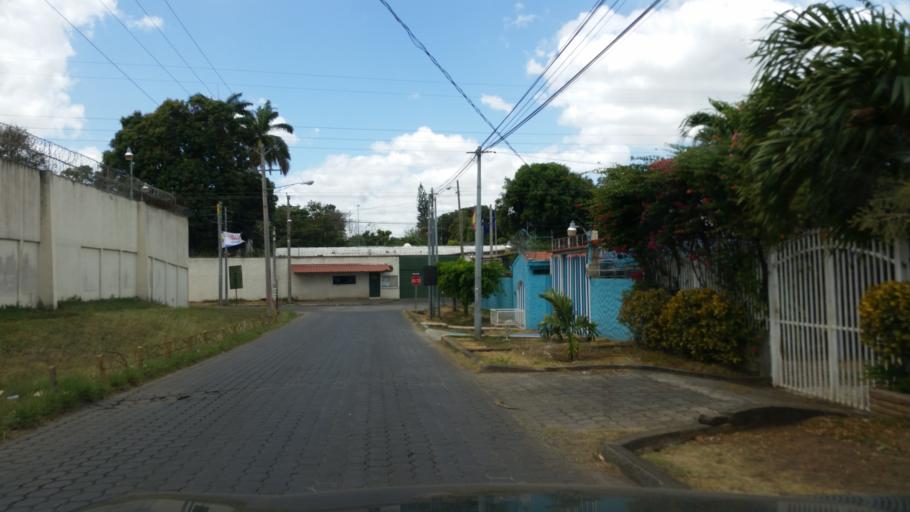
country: NI
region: Managua
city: Managua
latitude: 12.0988
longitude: -86.2320
